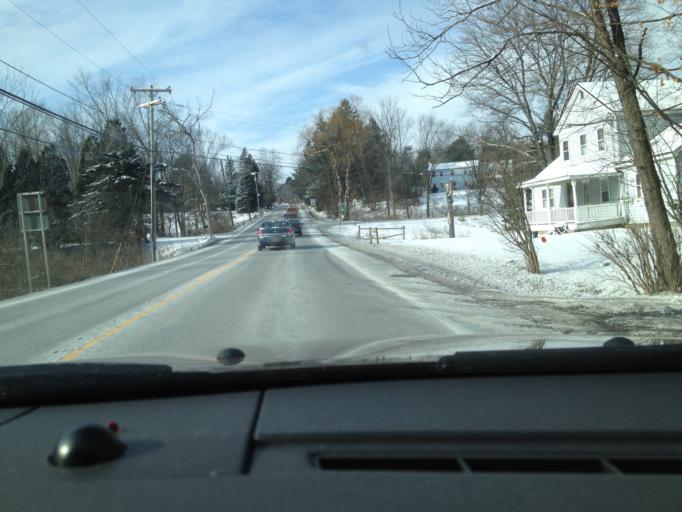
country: US
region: New York
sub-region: Rensselaer County
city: Wynantskill
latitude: 42.6515
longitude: -73.6669
